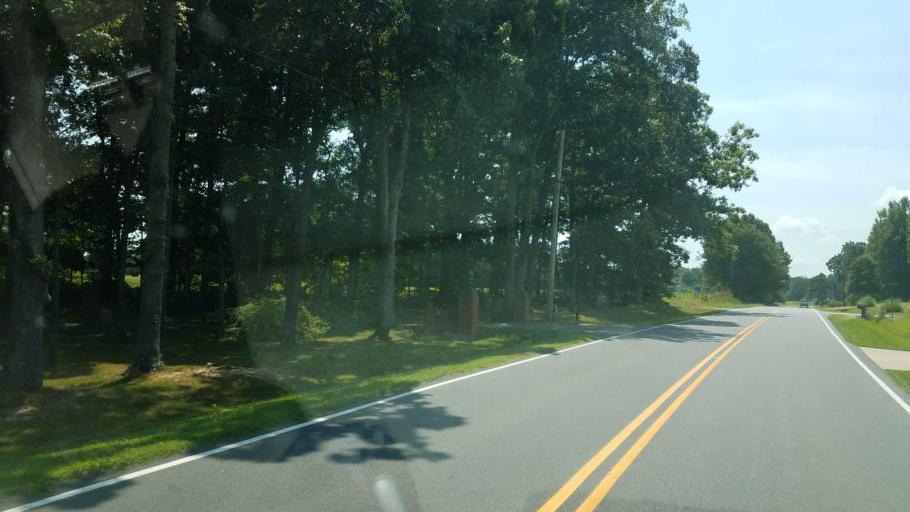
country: US
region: North Carolina
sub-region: Gaston County
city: Cherryville
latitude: 35.3584
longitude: -81.3587
